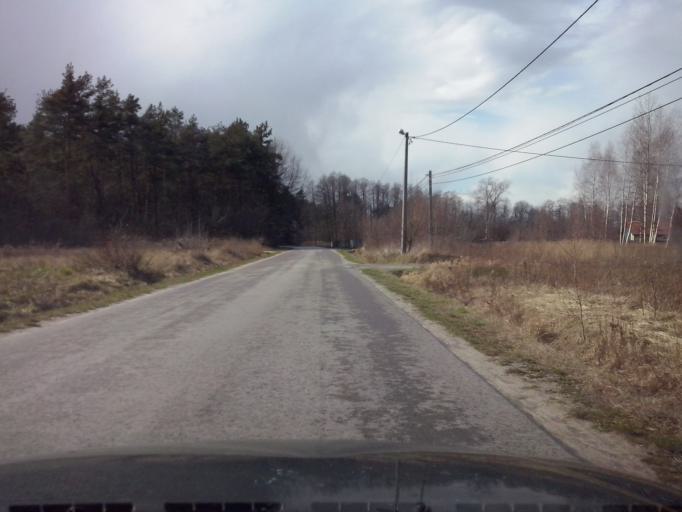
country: PL
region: Subcarpathian Voivodeship
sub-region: Powiat nizanski
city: Krzeszow
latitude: 50.4143
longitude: 22.3407
